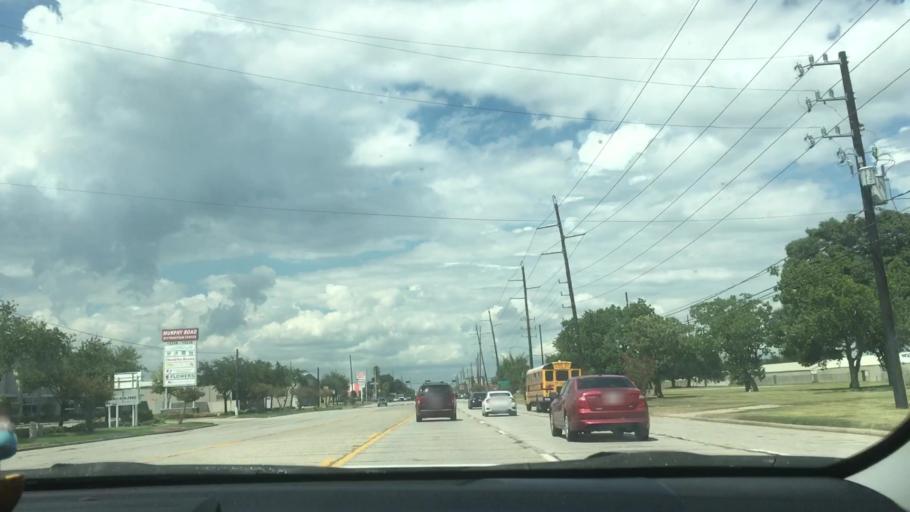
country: US
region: Texas
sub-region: Fort Bend County
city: Stafford
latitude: 29.6299
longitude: -95.5649
